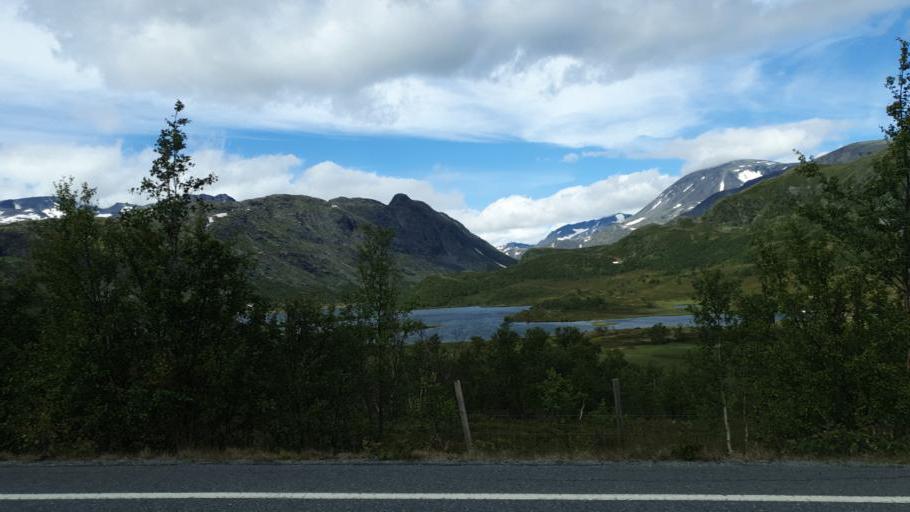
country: NO
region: Oppland
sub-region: Oystre Slidre
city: Heggenes
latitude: 61.4759
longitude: 8.8225
